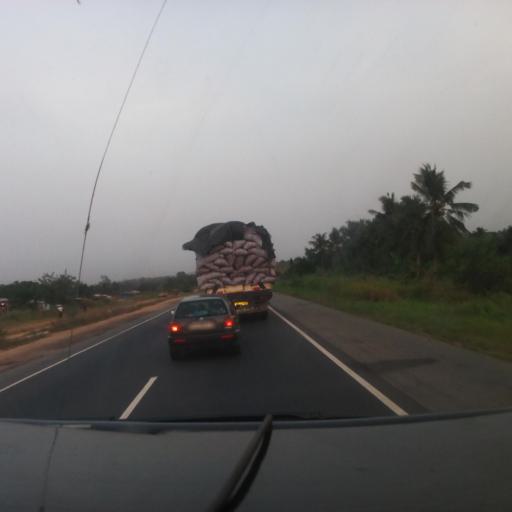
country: GH
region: Eastern
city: Nsawam
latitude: 5.8948
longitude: -0.3850
